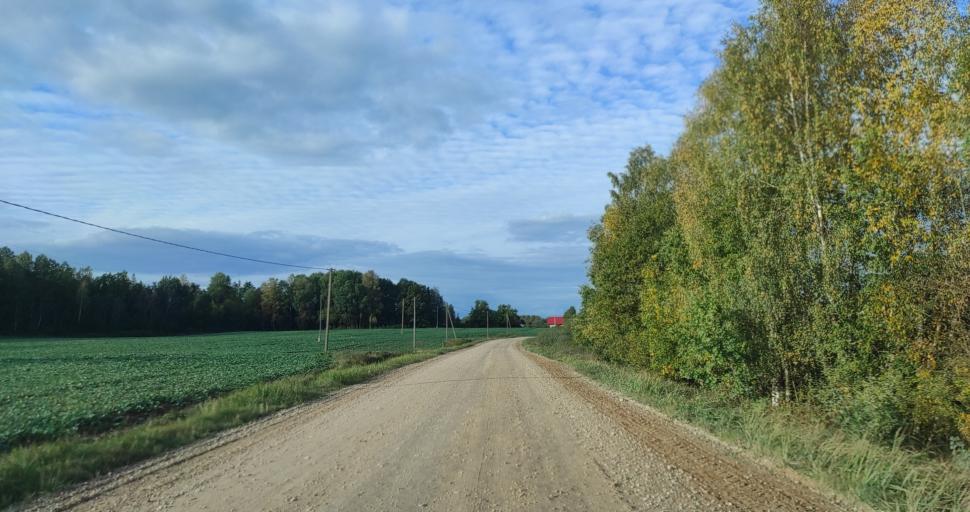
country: LV
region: Skrunda
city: Skrunda
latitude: 56.7470
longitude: 21.8162
